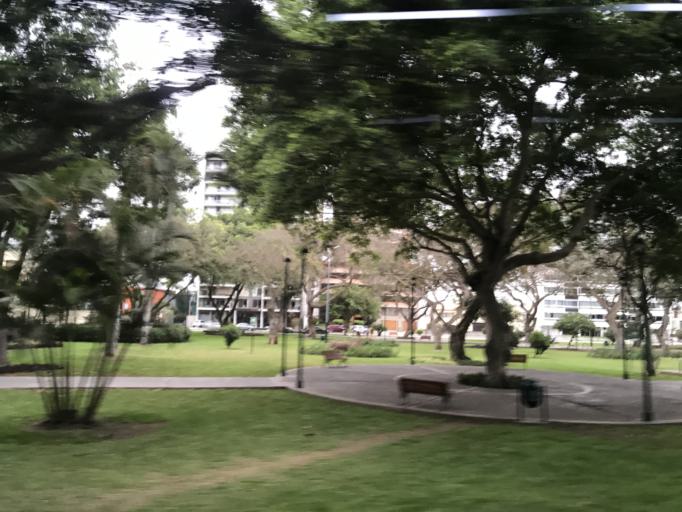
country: PE
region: Lima
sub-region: Lima
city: San Isidro
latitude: -12.0954
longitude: -77.0483
